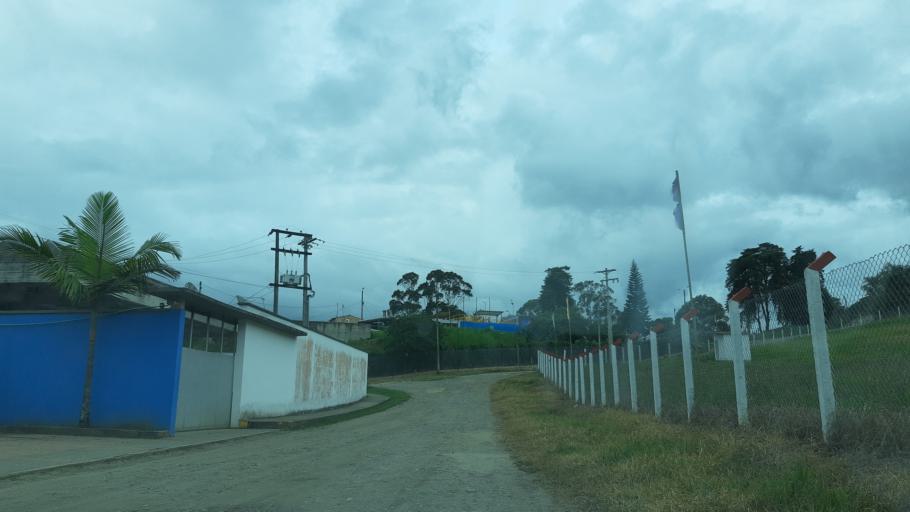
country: CO
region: Boyaca
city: Garagoa
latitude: 5.0817
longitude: -73.3598
